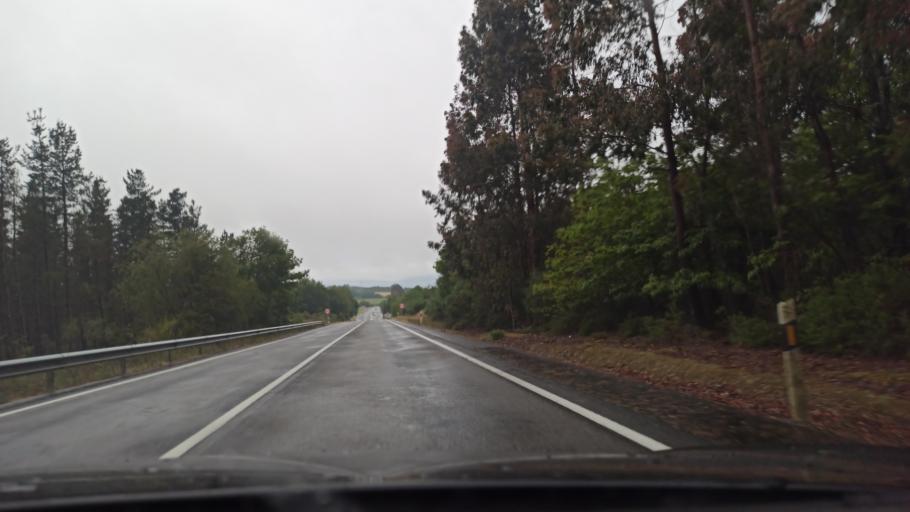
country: ES
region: Galicia
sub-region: Provincia de Lugo
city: Monterroso
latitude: 42.8139
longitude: -7.7677
